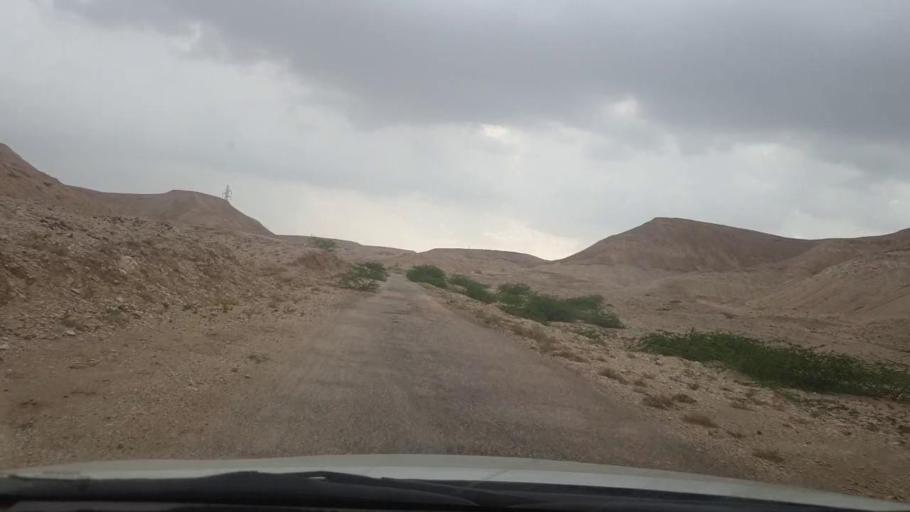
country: PK
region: Sindh
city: Khairpur
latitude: 27.4706
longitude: 68.9114
